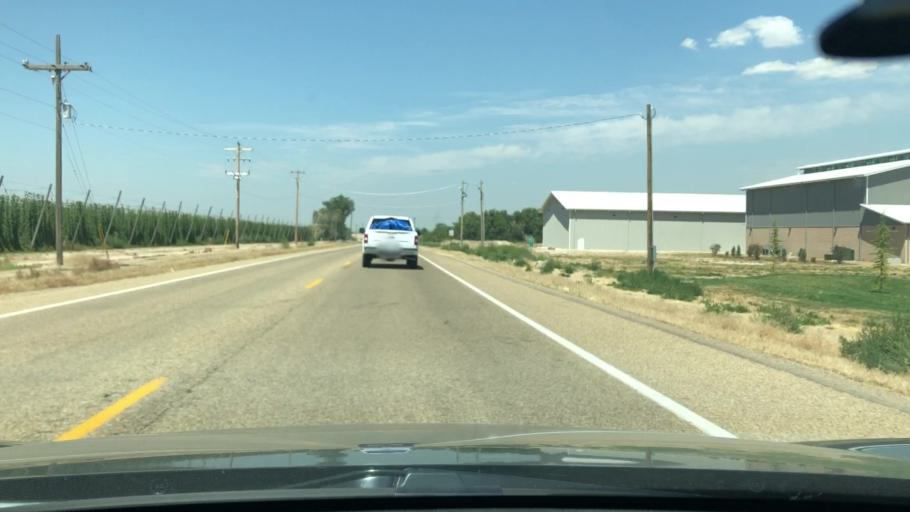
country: US
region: Idaho
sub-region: Canyon County
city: Wilder
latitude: 43.7054
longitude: -116.9120
